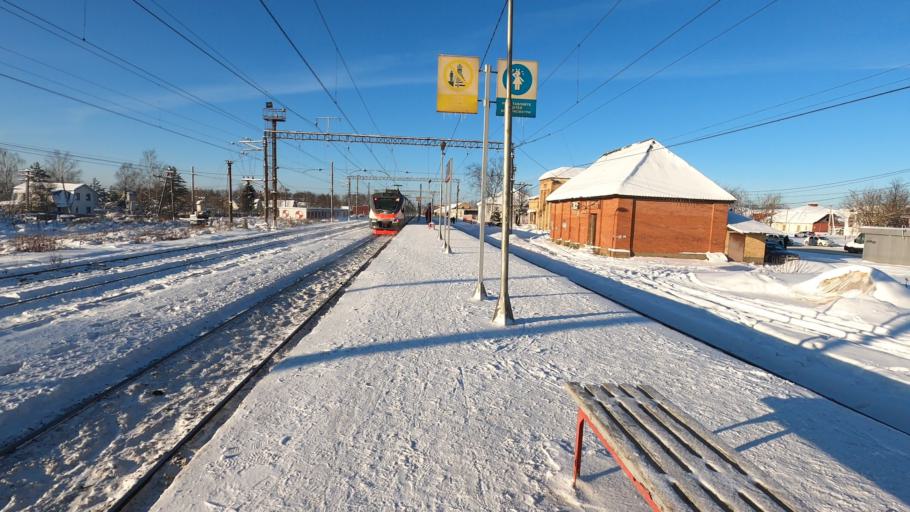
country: RU
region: Moskovskaya
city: Taldom
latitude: 56.7220
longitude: 37.5270
